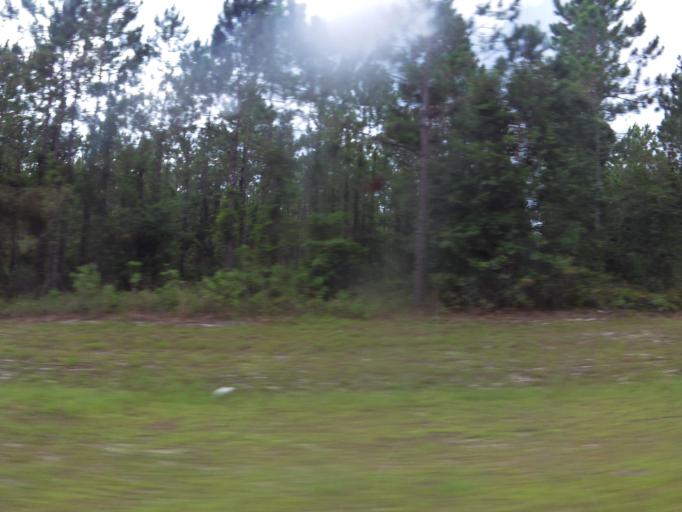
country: US
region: Georgia
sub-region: Camden County
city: Kingsland
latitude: 30.7667
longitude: -81.6493
